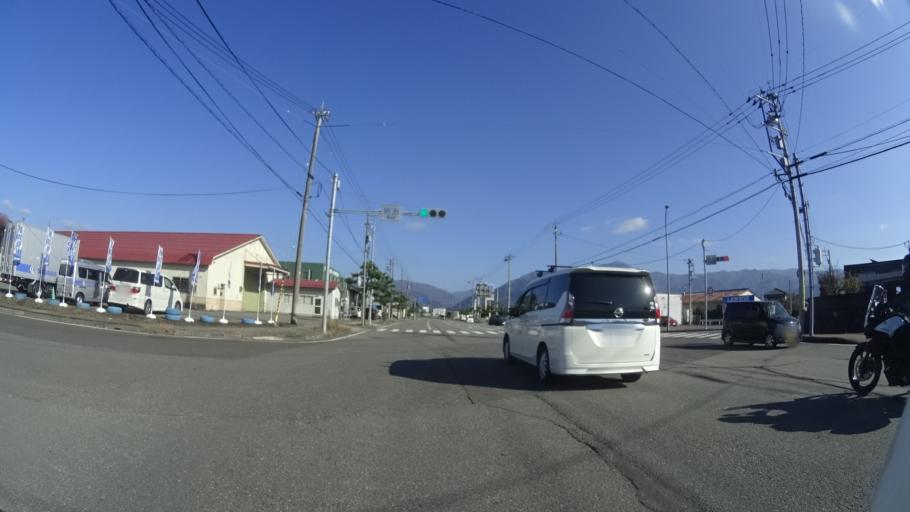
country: JP
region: Fukui
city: Ono
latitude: 35.9702
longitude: 136.5008
